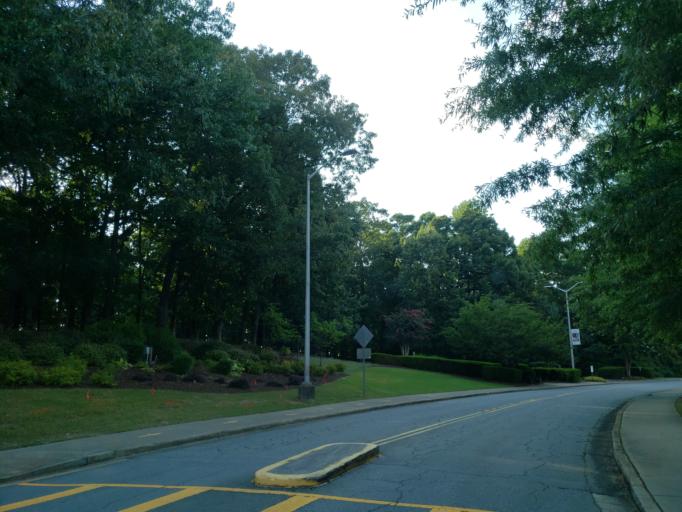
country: US
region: Georgia
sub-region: Cobb County
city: Kennesaw
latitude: 34.0420
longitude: -84.5843
